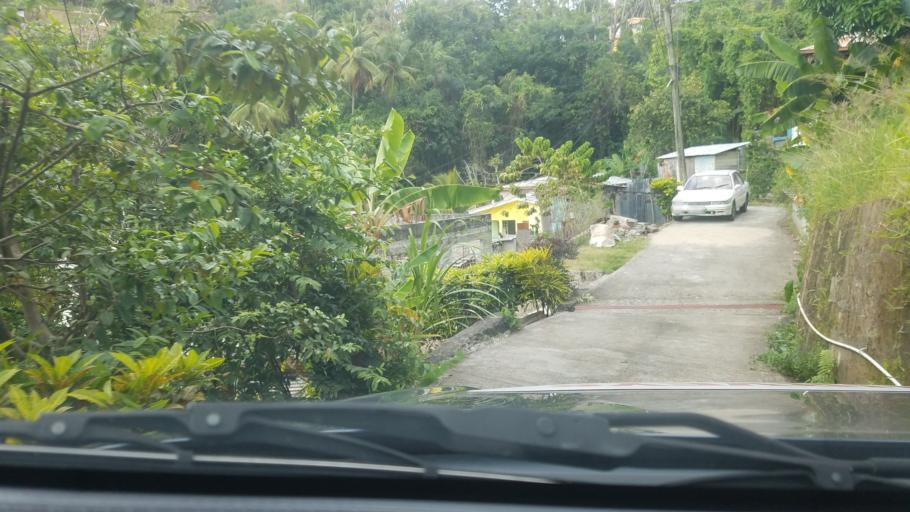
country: LC
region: Castries Quarter
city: Bisee
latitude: 14.0116
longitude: -60.9811
